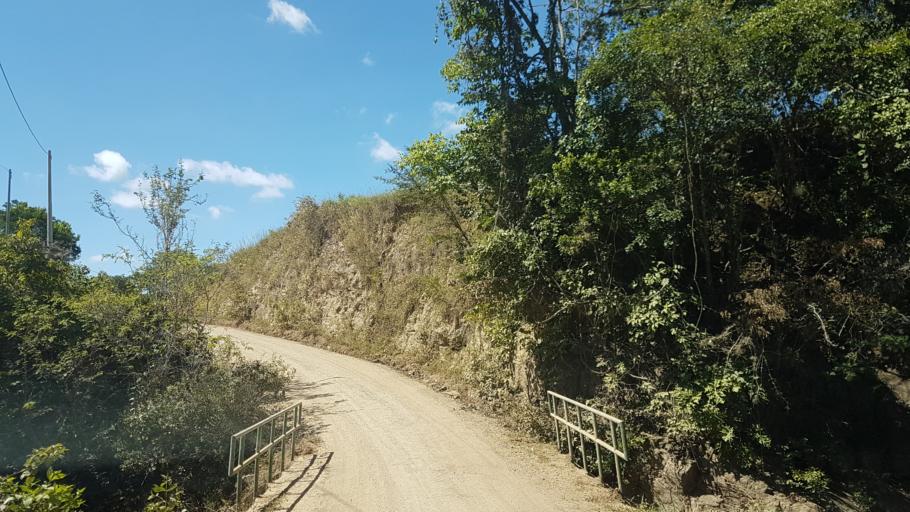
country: HN
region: El Paraiso
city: Santa Cruz
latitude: 13.7323
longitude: -86.6825
